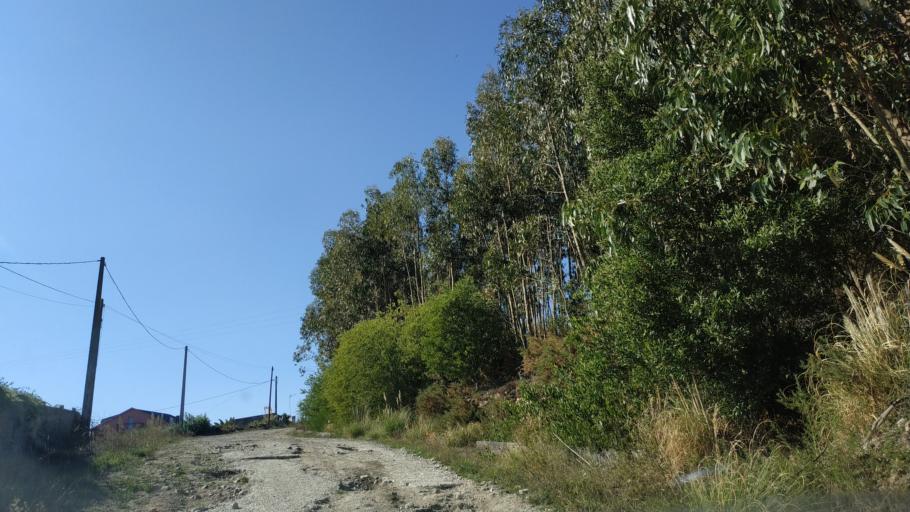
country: ES
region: Galicia
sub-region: Provincia da Coruna
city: Culleredo
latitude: 43.3218
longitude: -8.3881
